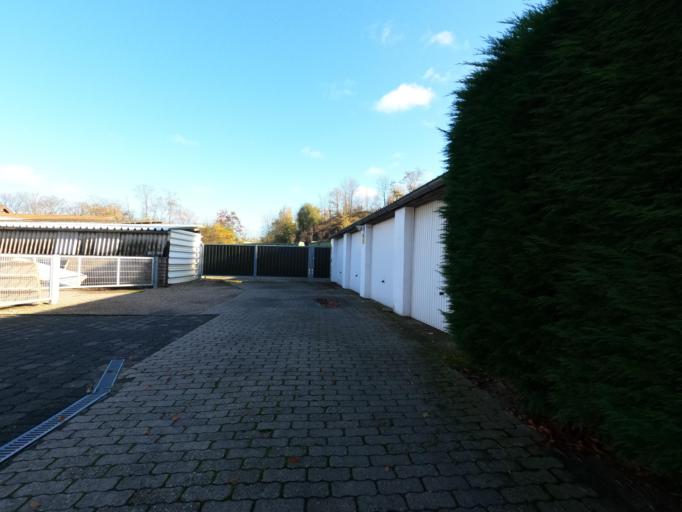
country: DE
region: North Rhine-Westphalia
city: Huckelhoven
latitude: 51.0563
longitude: 6.2021
